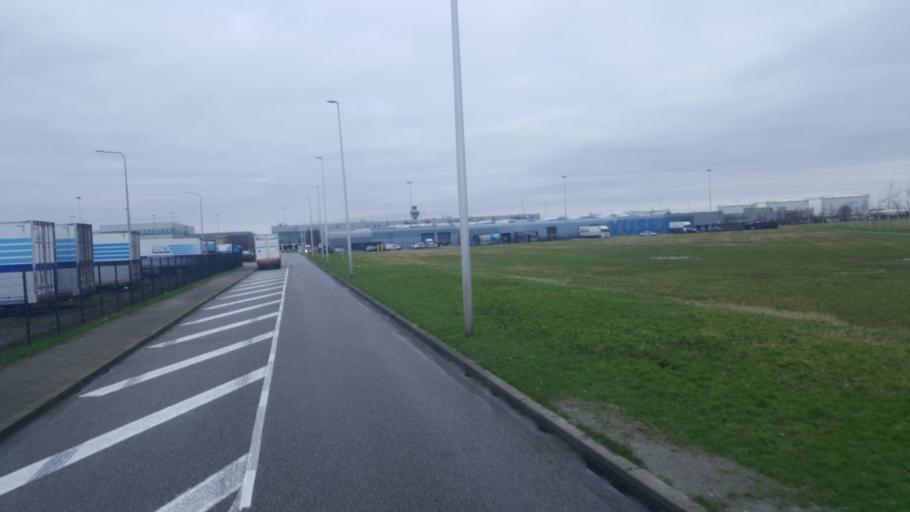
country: NL
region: North Holland
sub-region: Gemeente Aalsmeer
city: Aalsmeer
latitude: 52.2926
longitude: 4.7722
